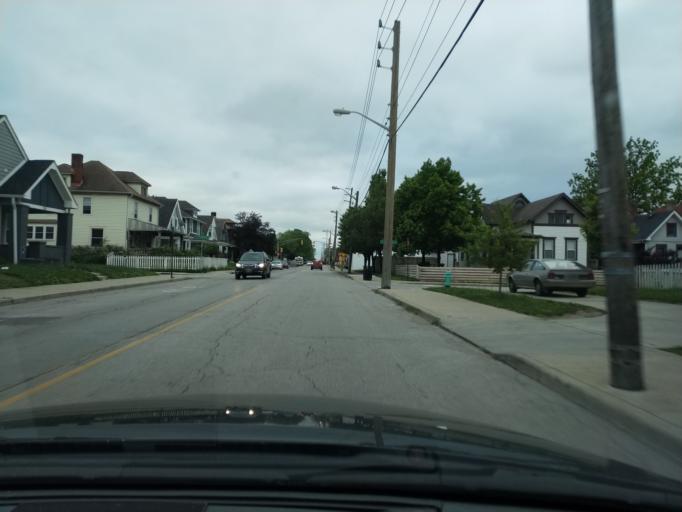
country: US
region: Indiana
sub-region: Marion County
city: Indianapolis
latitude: 39.7493
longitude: -86.1495
